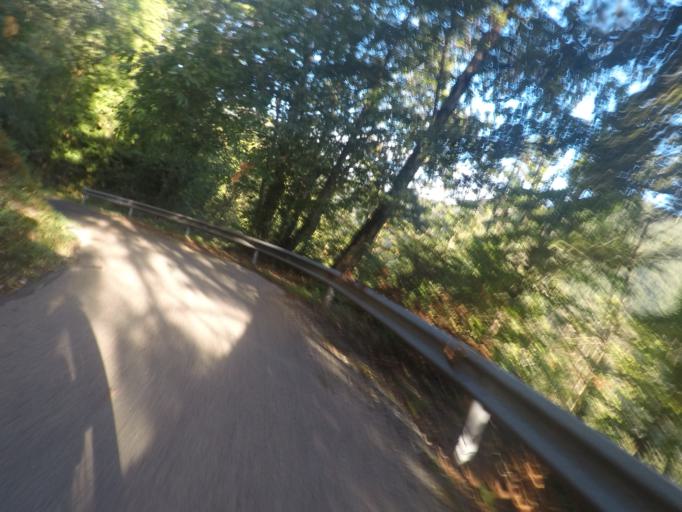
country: IT
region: Tuscany
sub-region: Provincia di Lucca
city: Pescaglia
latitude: 43.9403
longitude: 10.3960
